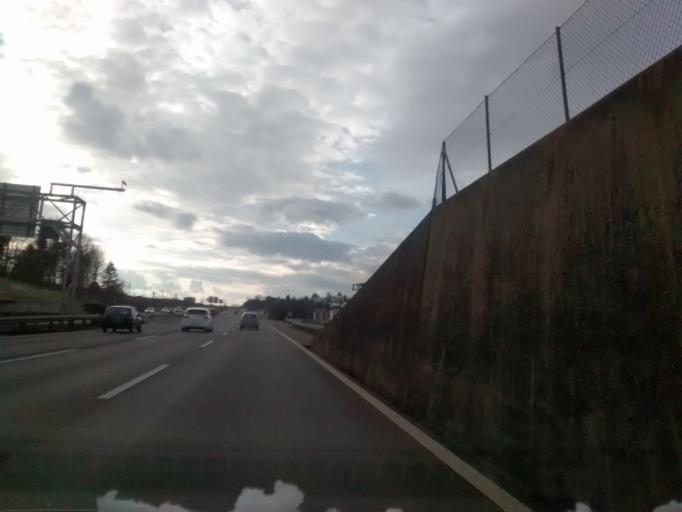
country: CH
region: Vaud
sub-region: Ouest Lausannois District
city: Ecublens
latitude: 46.5381
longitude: 6.5549
